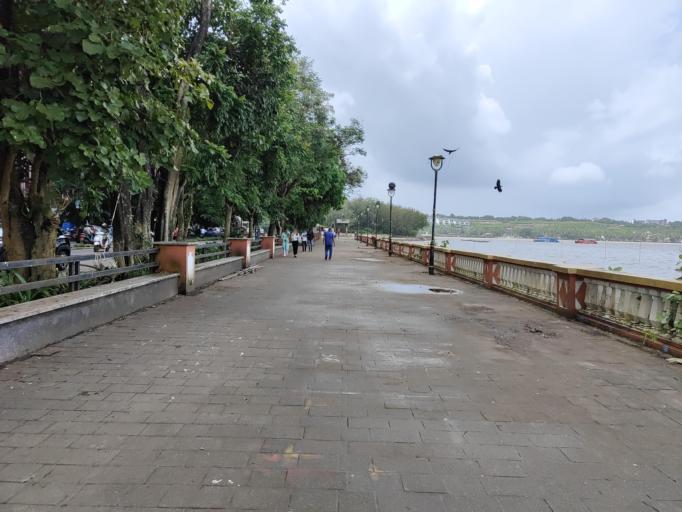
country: IN
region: Goa
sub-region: North Goa
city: Panaji
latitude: 15.5007
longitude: 73.8225
